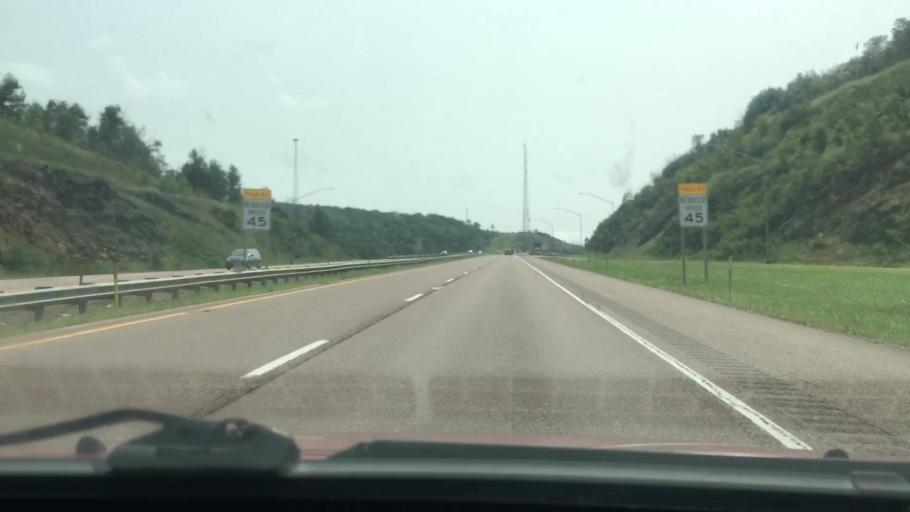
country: US
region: Maryland
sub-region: Allegany County
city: Frostburg
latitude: 39.6819
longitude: -78.9690
